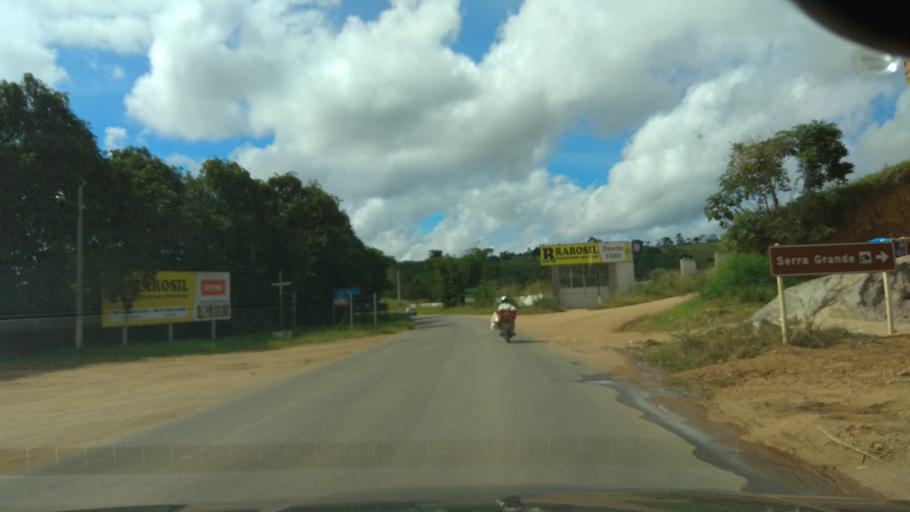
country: BR
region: Bahia
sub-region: Mutuipe
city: Mutuipe
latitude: -13.2288
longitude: -39.4942
